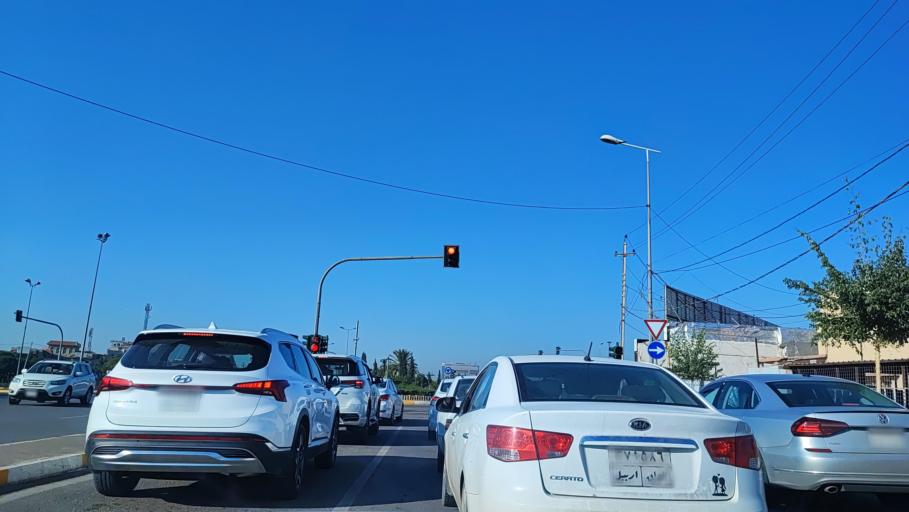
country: IQ
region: Arbil
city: Erbil
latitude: 36.1803
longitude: 44.0093
